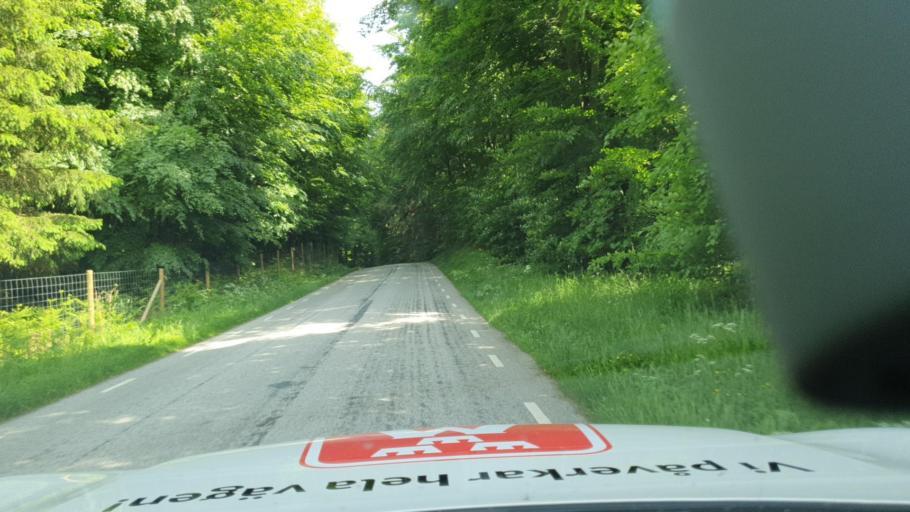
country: SE
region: Skane
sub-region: Svedala Kommun
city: Svedala
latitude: 55.5346
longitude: 13.2803
